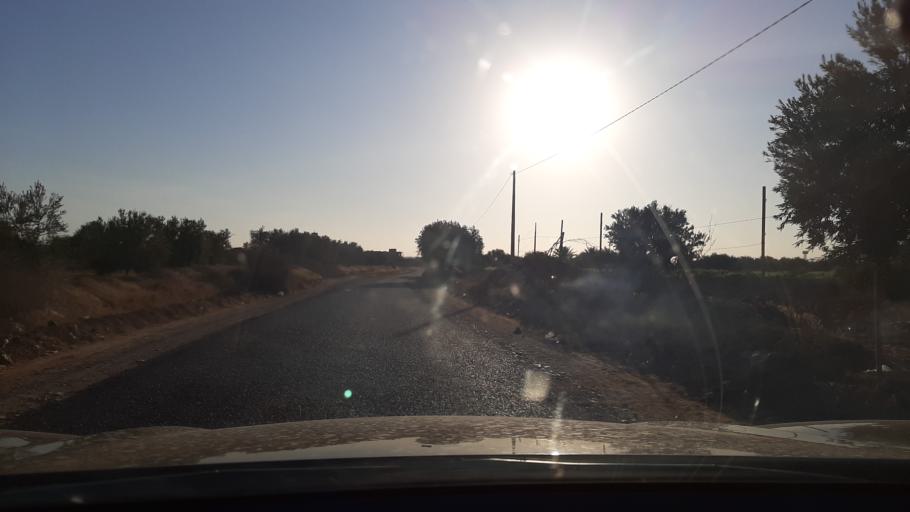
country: TN
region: Qabis
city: Matmata
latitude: 33.6174
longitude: 10.2532
